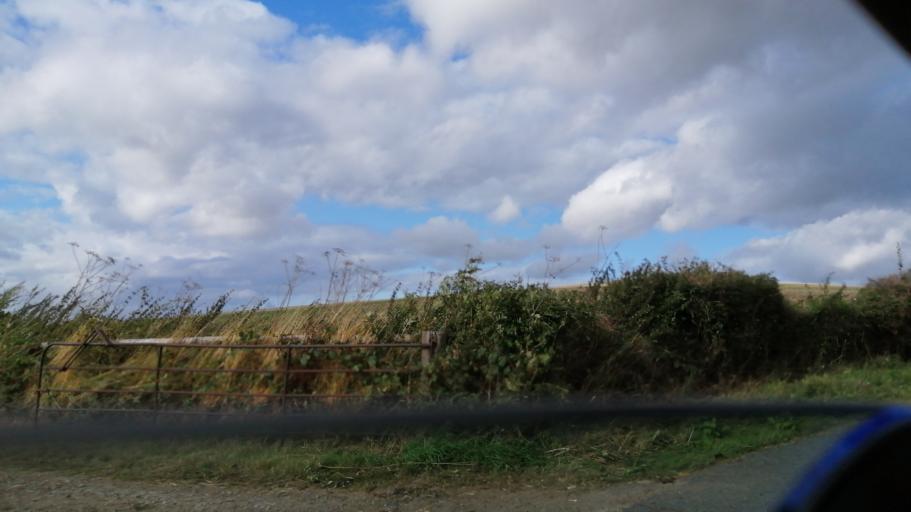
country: GB
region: England
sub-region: Herefordshire
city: Callow
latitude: 52.0075
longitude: -2.7629
